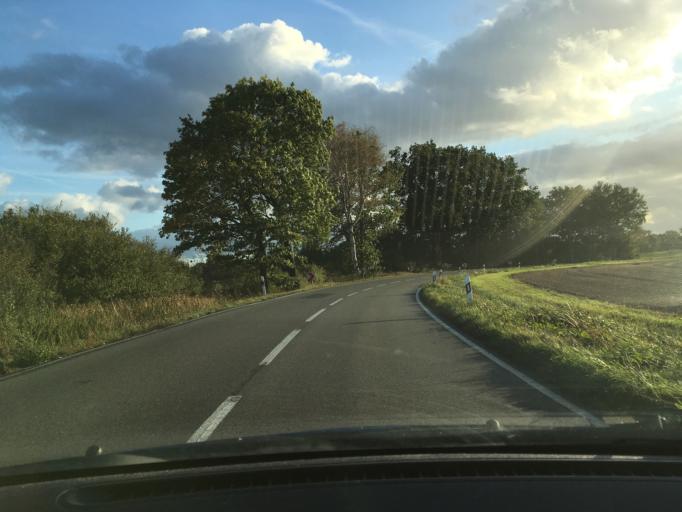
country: DE
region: Lower Saxony
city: Hittbergen
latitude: 53.3321
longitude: 10.5991
